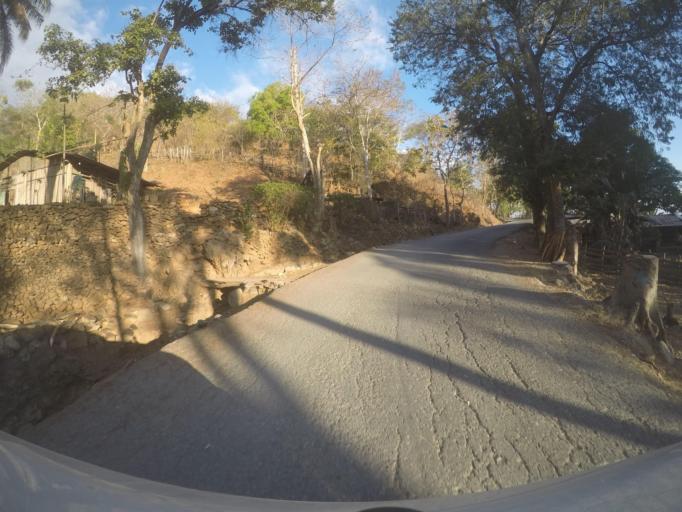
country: TL
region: Bobonaro
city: Maliana
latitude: -8.9597
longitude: 125.0293
